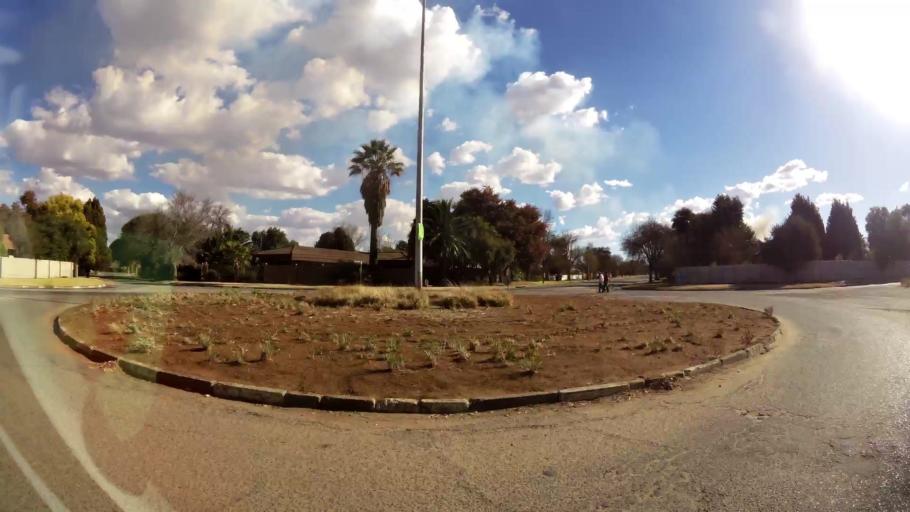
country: ZA
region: North-West
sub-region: Dr Kenneth Kaunda District Municipality
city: Klerksdorp
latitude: -26.8303
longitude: 26.6623
